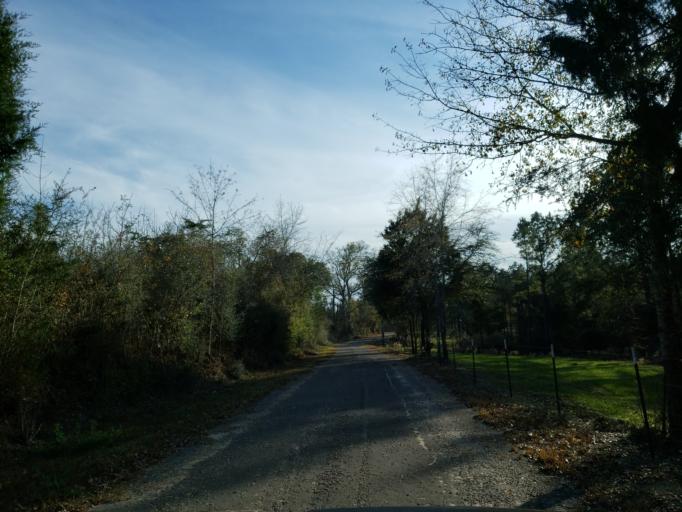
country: US
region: Mississippi
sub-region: Wayne County
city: Belmont
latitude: 31.4308
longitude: -88.4750
